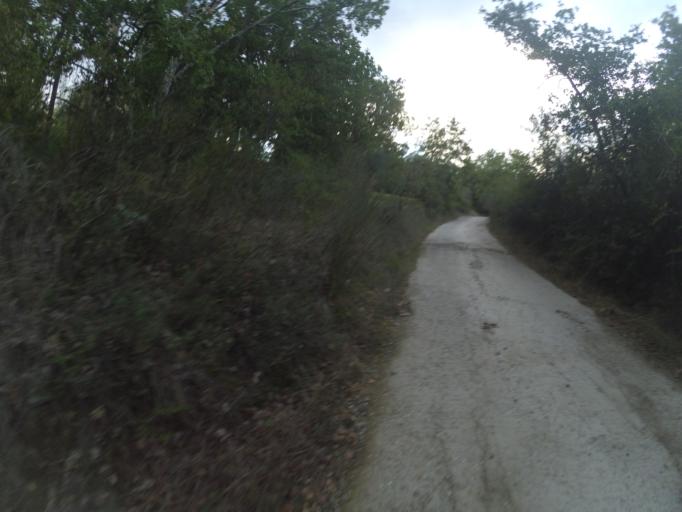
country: IT
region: Tuscany
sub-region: Province of Arezzo
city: Castiglion Fibocchi
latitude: 43.5424
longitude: 11.7677
